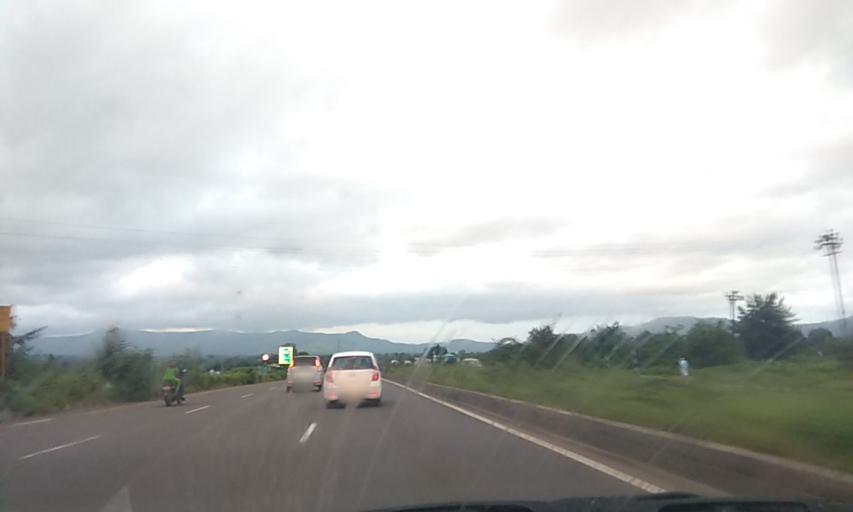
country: IN
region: Maharashtra
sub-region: Satara Division
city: Wai
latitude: 17.9341
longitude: 73.9765
